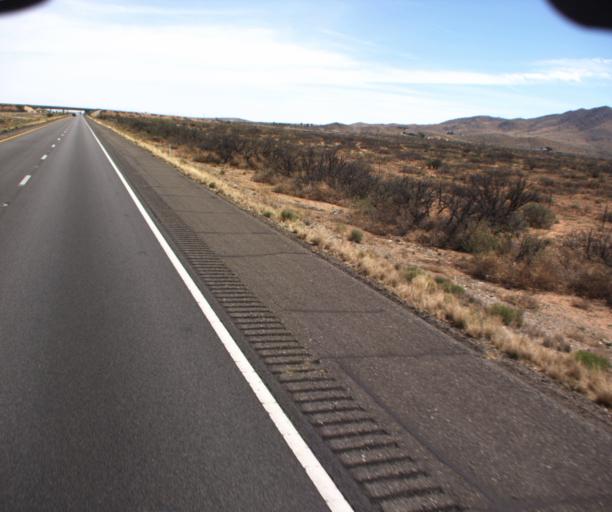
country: US
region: Arizona
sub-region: Cochise County
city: Willcox
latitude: 32.3010
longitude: -109.8047
